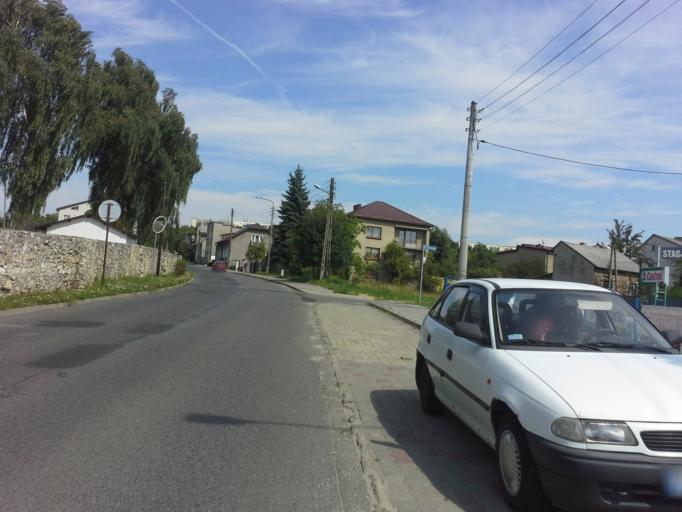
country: PL
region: Lesser Poland Voivodeship
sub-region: Powiat chrzanowski
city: Trzebinia
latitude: 50.1552
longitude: 19.4712
